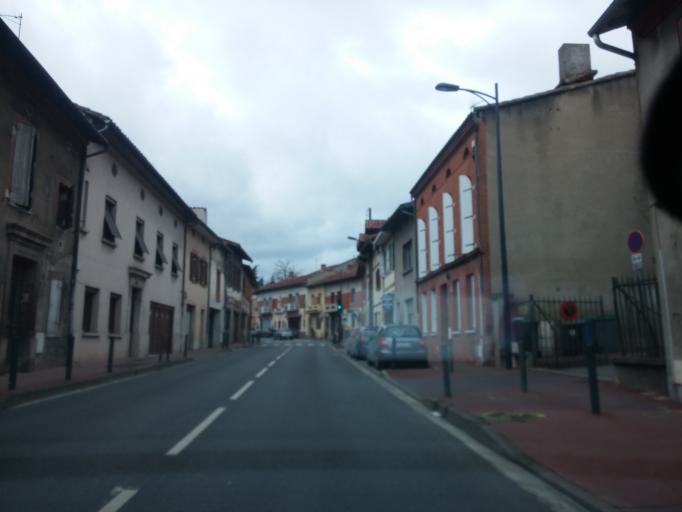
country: FR
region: Midi-Pyrenees
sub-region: Departement de la Haute-Garonne
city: Blagnac
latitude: 43.6085
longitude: 1.3817
